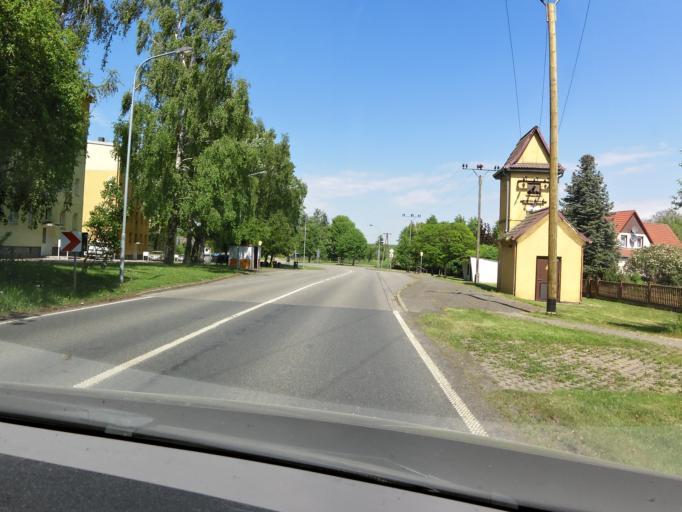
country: DE
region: Thuringia
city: Klettstedt
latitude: 51.1427
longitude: 10.7423
